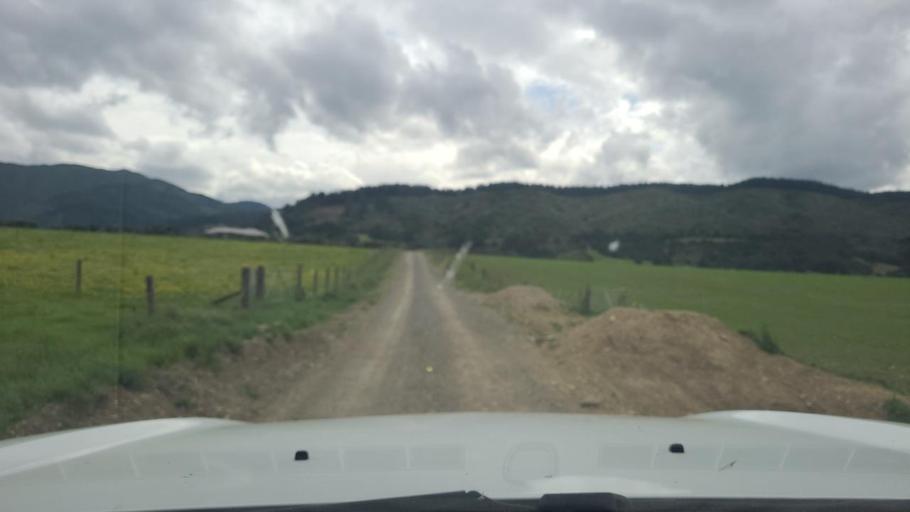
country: NZ
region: Wellington
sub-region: Masterton District
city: Masterton
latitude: -41.0100
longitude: 175.4782
